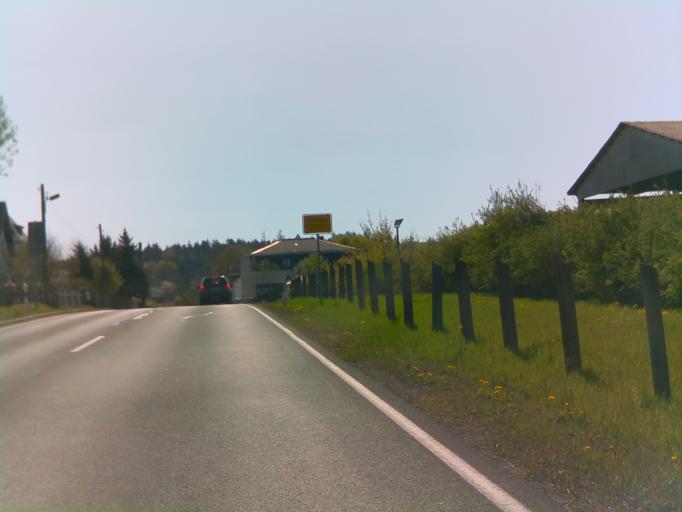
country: DE
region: Saxony
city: Mehltheuer
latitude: 50.5455
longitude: 12.0323
